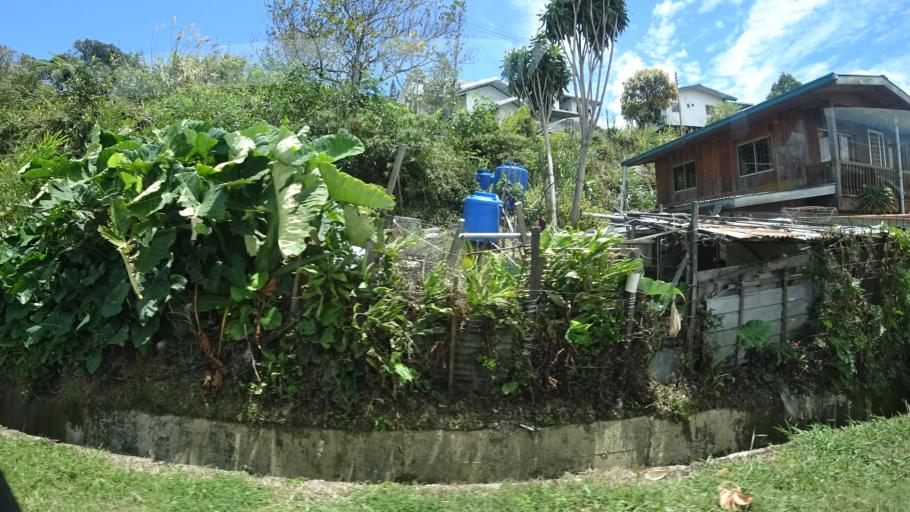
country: MY
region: Sabah
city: Ranau
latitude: 5.9814
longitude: 116.5611
